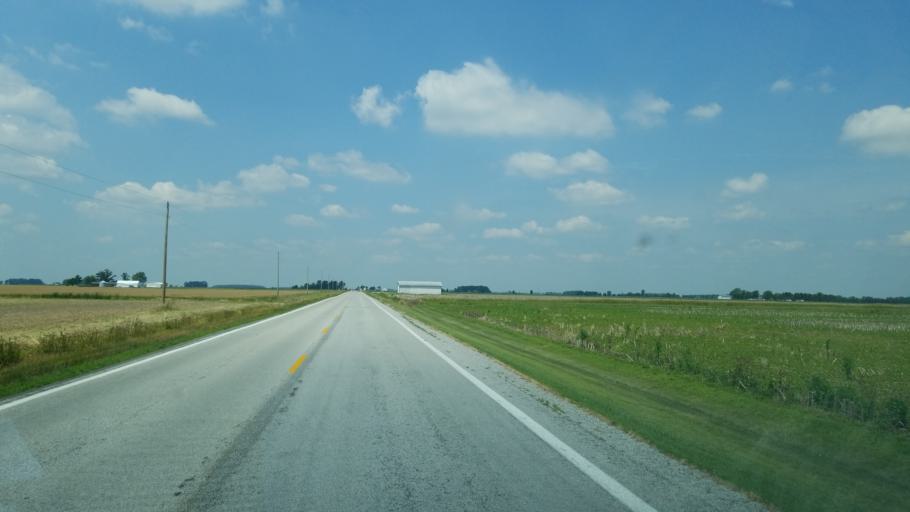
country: US
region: Ohio
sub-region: Henry County
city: Deshler
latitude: 41.2839
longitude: -83.9298
